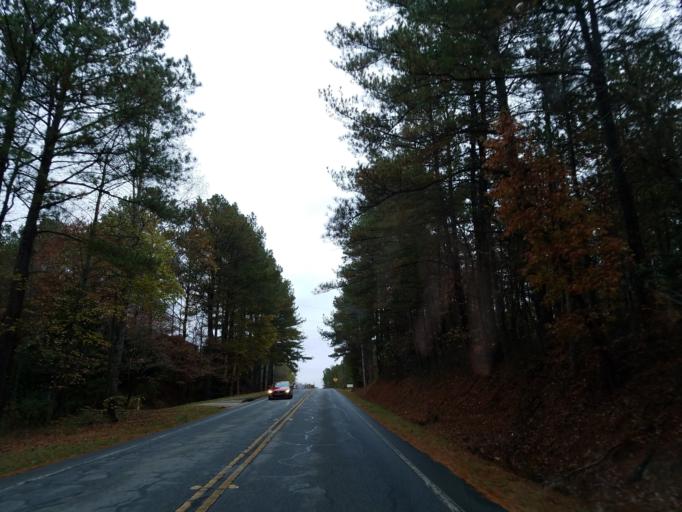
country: US
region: Georgia
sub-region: Cherokee County
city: Canton
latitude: 34.3061
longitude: -84.5559
